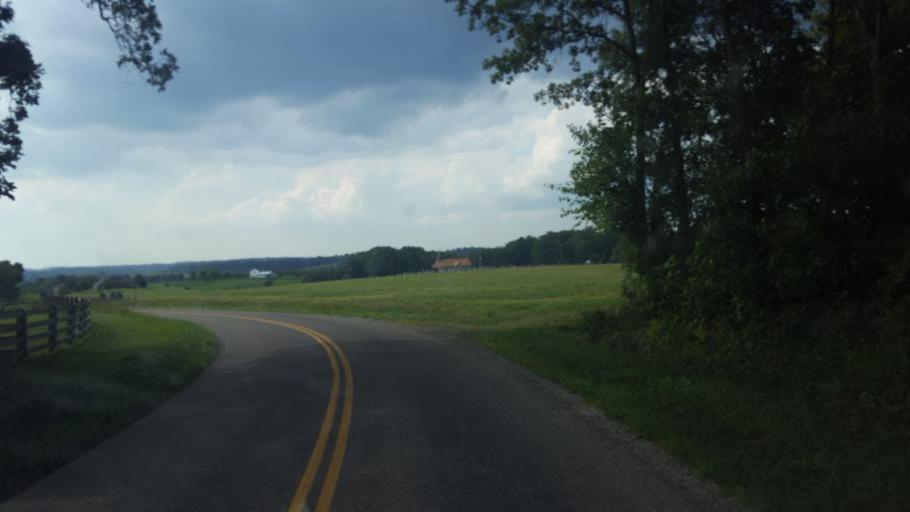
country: US
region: Ohio
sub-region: Knox County
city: Gambier
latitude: 40.3399
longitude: -82.3538
